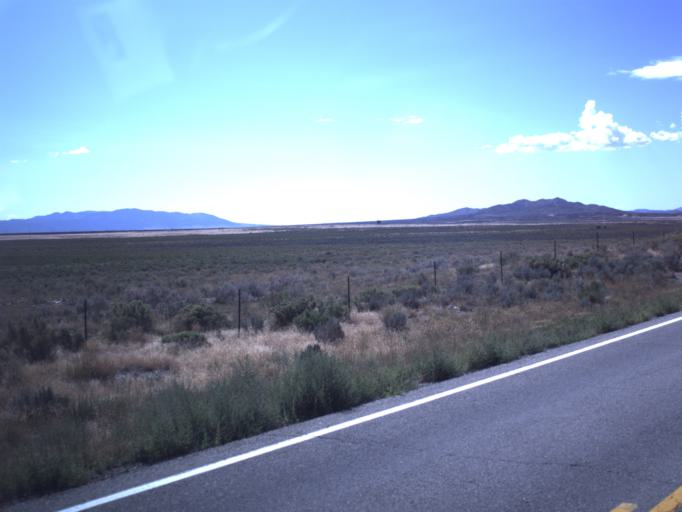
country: US
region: Utah
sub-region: Tooele County
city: Tooele
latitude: 40.2124
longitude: -112.4071
